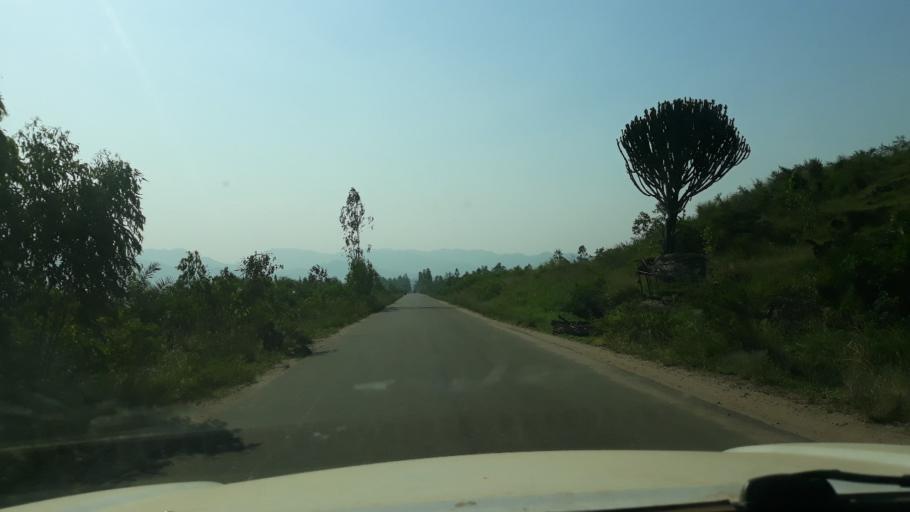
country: BI
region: Cibitoke
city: Cibitoke
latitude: -2.8233
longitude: 29.0094
